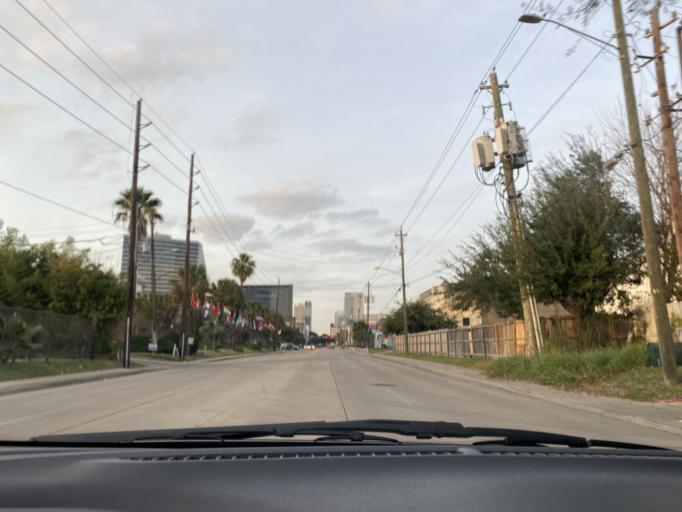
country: US
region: Texas
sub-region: Harris County
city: Bunker Hill Village
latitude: 29.7339
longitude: -95.5596
